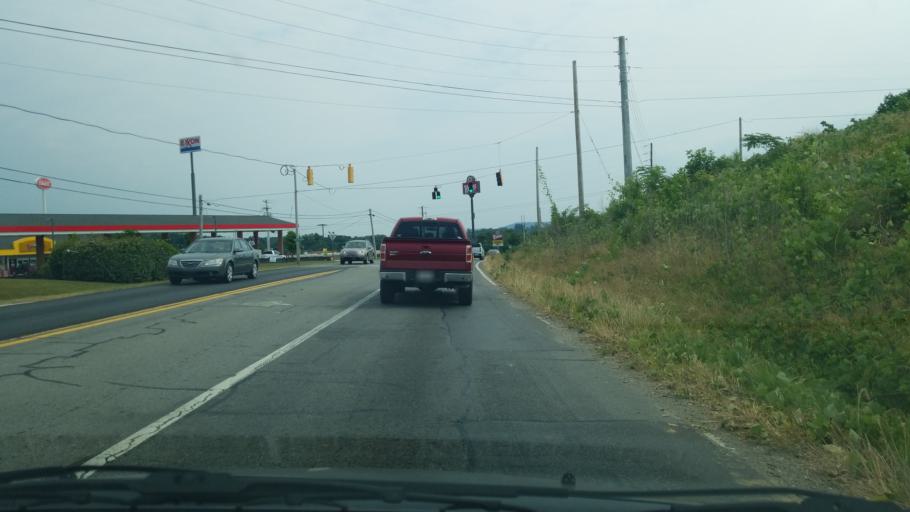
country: US
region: Georgia
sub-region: Catoosa County
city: Ringgold
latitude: 34.9059
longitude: -85.1308
